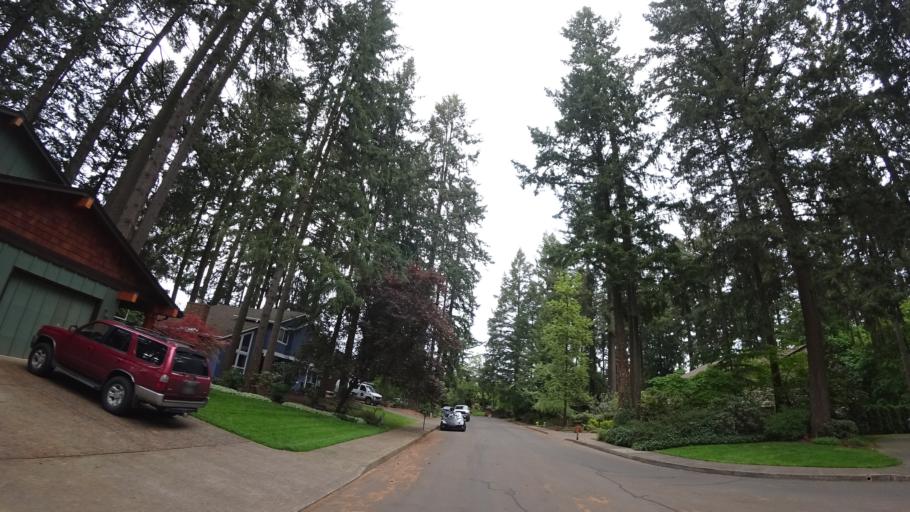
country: US
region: Oregon
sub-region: Washington County
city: Hillsboro
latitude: 45.4904
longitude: -122.9567
